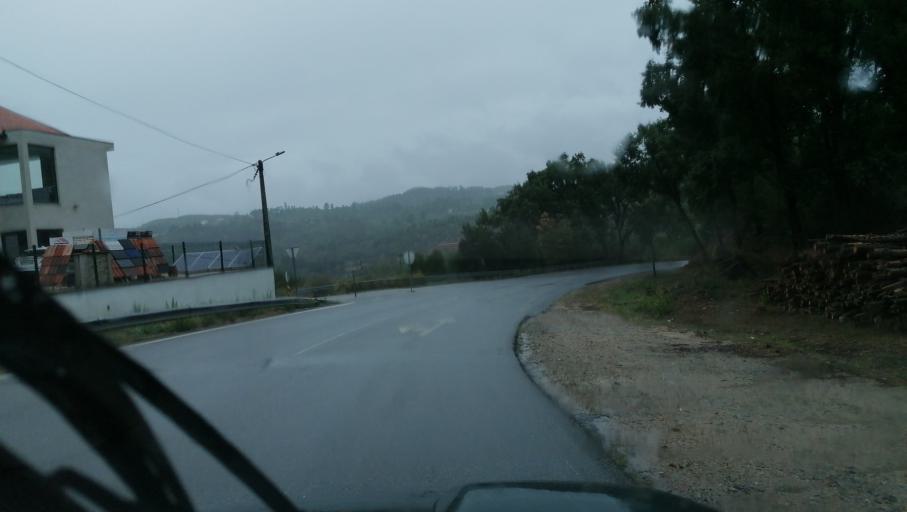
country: PT
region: Braga
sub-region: Cabeceiras de Basto
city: Cabeceiras de Basto
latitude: 41.4897
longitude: -7.9378
